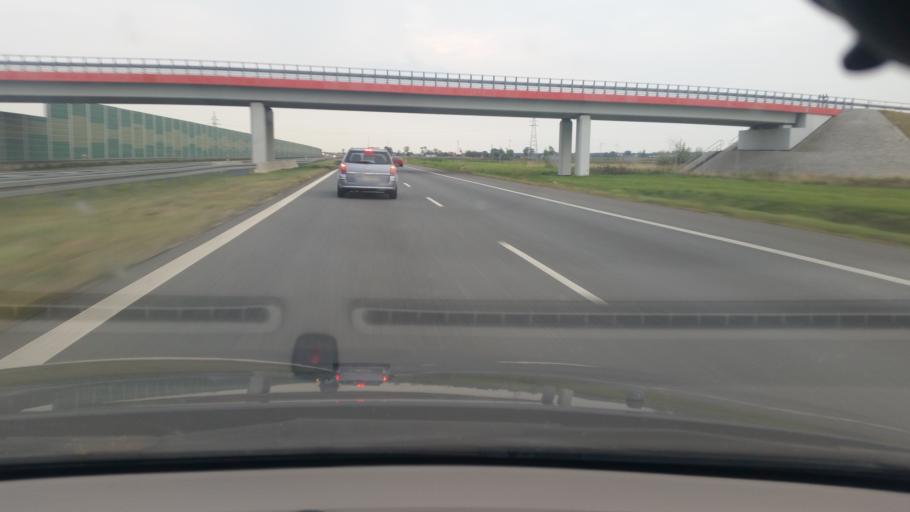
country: PL
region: Lodz Voivodeship
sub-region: Powiat kutnowski
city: Krzyzanow
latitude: 52.2442
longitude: 19.4493
